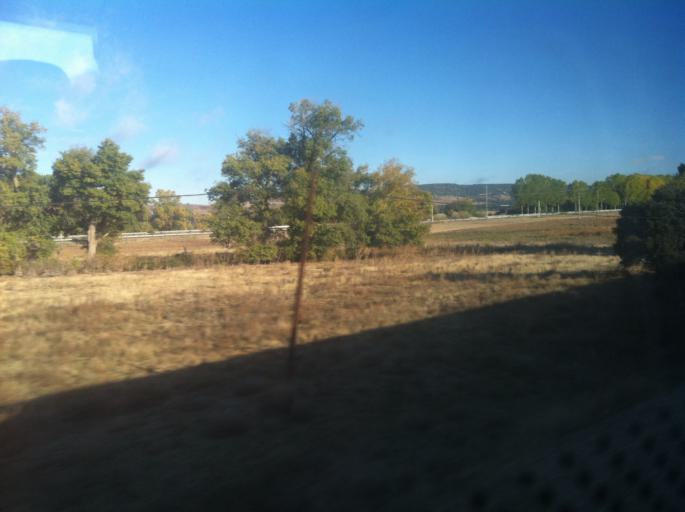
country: ES
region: Castille and Leon
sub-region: Provincia de Palencia
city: Cordovilla la Real
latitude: 42.0536
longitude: -4.2399
